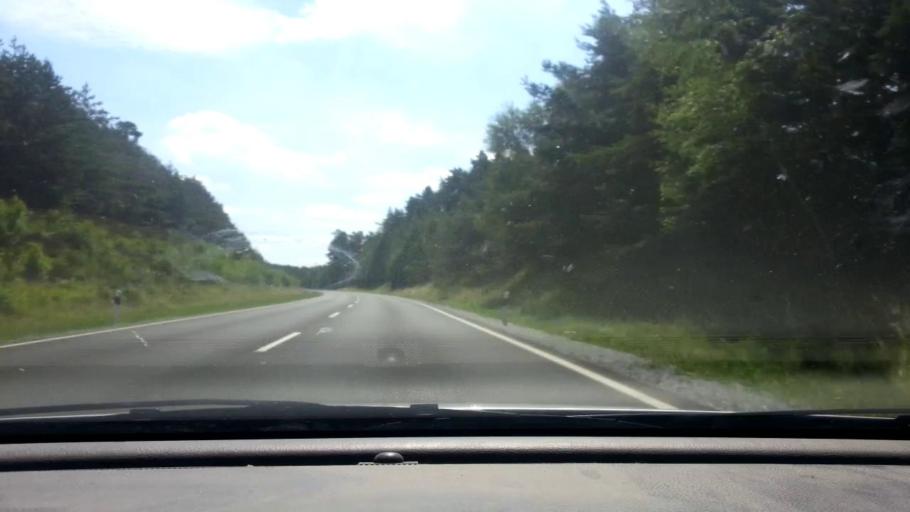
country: DE
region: Bavaria
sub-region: Upper Franconia
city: Seybothenreuth
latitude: 49.8876
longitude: 11.7192
